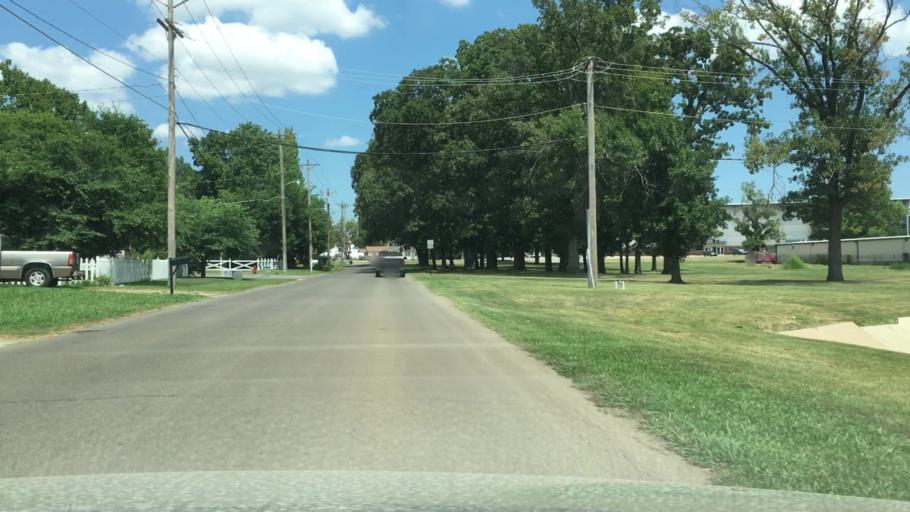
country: US
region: Oklahoma
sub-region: Cherokee County
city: Tahlequah
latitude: 35.9246
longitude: -94.9694
